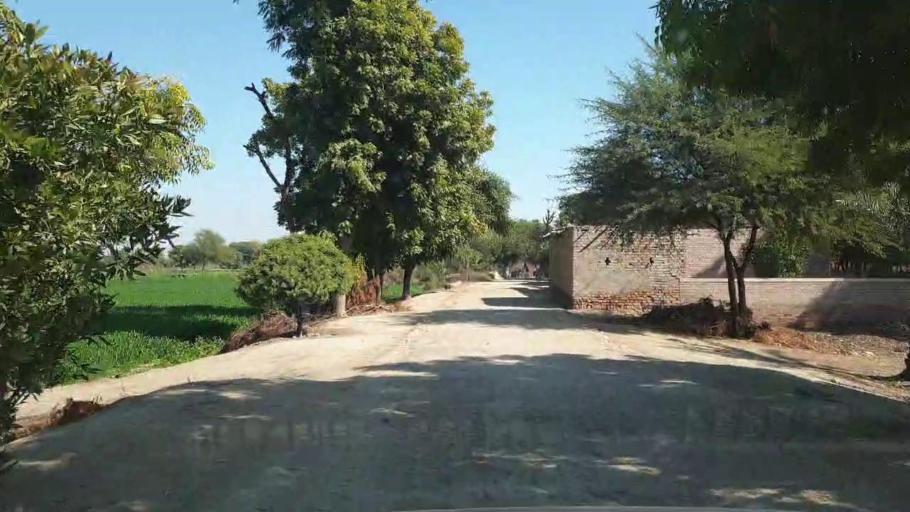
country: PK
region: Sindh
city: Shahpur Chakar
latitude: 26.1436
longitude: 68.6407
